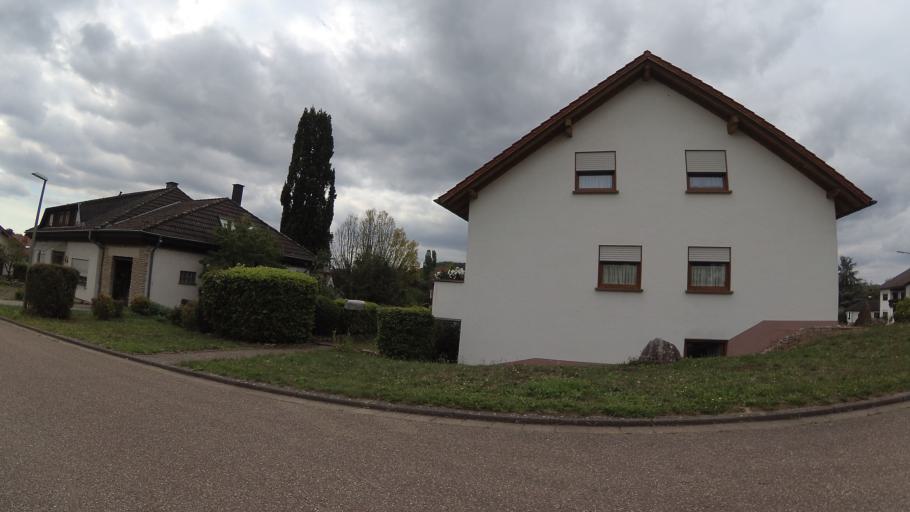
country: FR
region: Lorraine
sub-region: Departement de la Moselle
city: Sarreguemines
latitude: 49.1556
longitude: 7.1099
